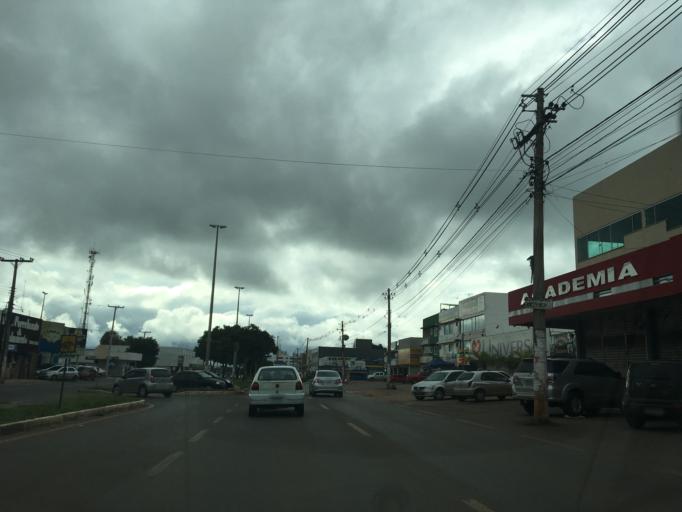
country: BR
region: Federal District
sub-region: Brasilia
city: Brasilia
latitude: -16.0049
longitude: -47.9942
